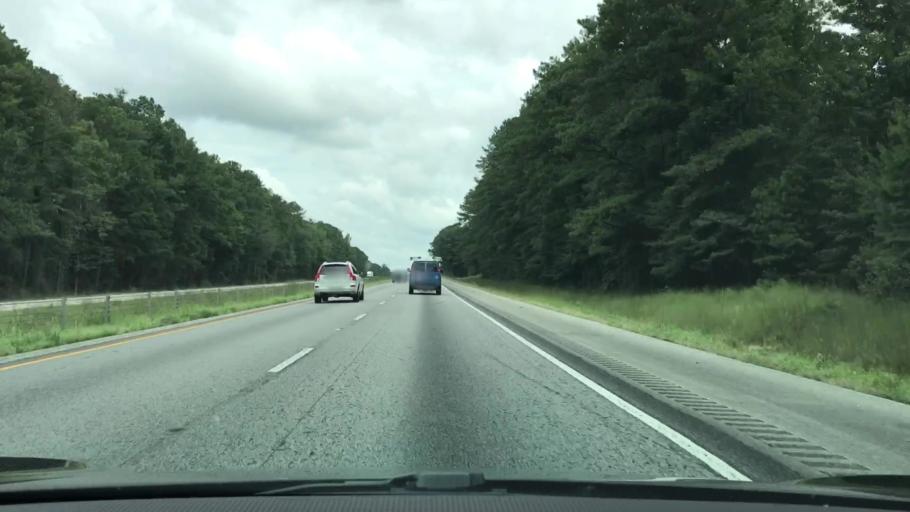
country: US
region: Alabama
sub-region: Chambers County
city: Huguley
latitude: 32.7613
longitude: -85.2673
